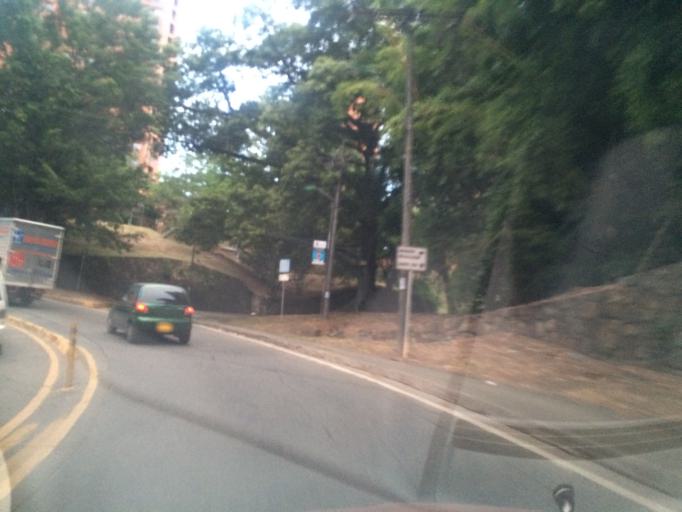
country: CO
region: Valle del Cauca
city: Cali
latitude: 3.4480
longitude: -76.5466
